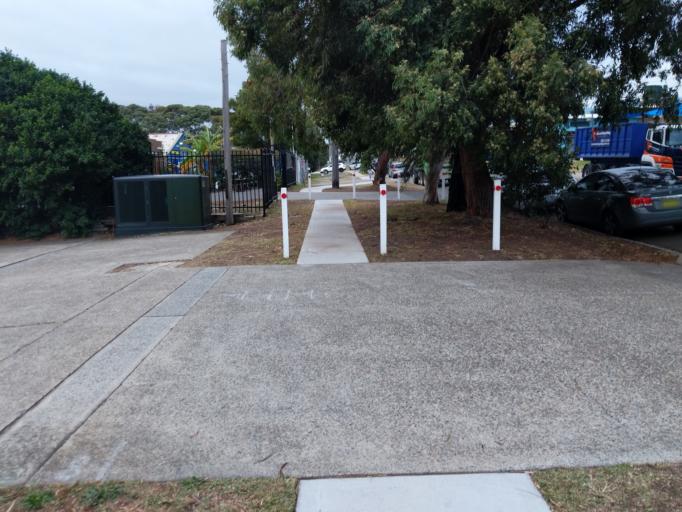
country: AU
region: New South Wales
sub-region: Sutherland Shire
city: Gymea
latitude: -34.0255
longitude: 151.0763
